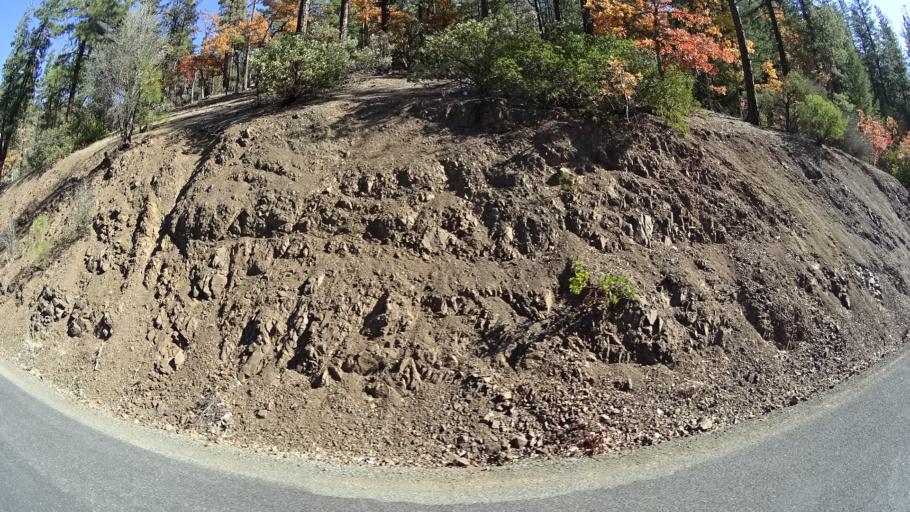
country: US
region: California
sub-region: Siskiyou County
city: Yreka
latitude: 41.6727
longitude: -122.8483
